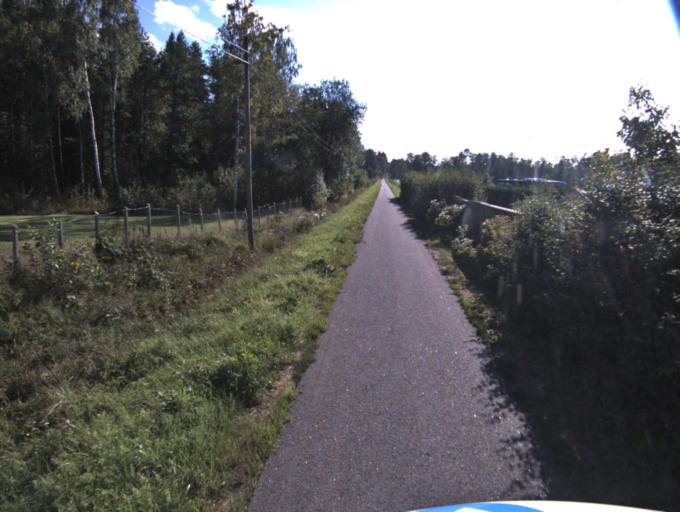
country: SE
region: Vaestra Goetaland
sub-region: Boras Kommun
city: Dalsjofors
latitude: 57.8229
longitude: 13.1565
